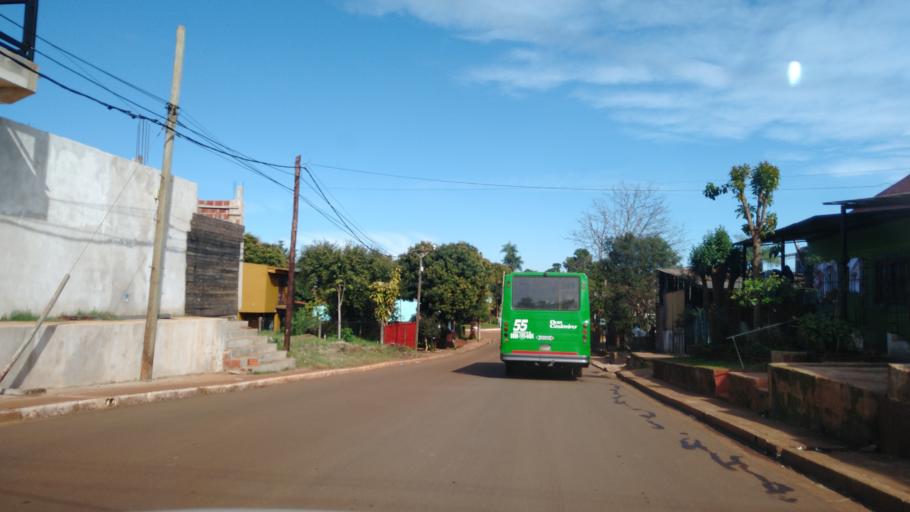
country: AR
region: Misiones
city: Garupa
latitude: -27.4653
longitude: -55.8561
